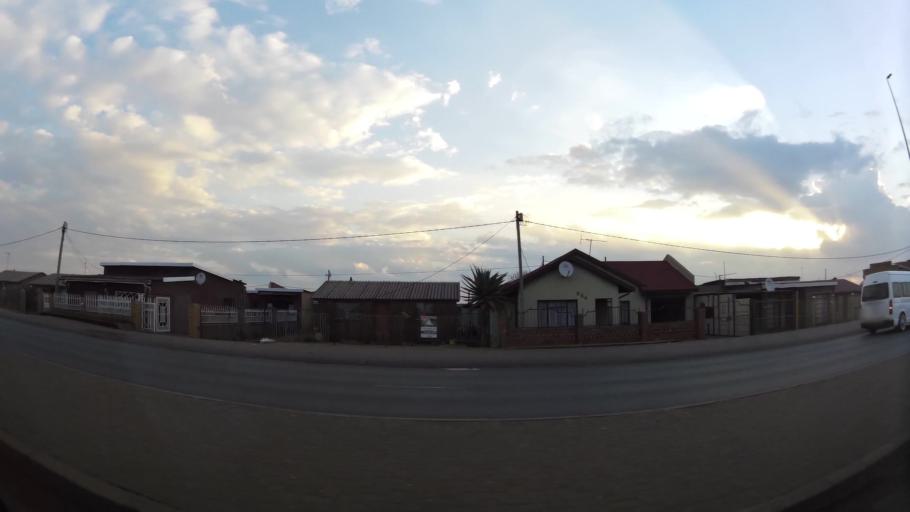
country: ZA
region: Gauteng
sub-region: City of Johannesburg Metropolitan Municipality
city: Orange Farm
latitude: -26.5709
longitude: 27.8376
